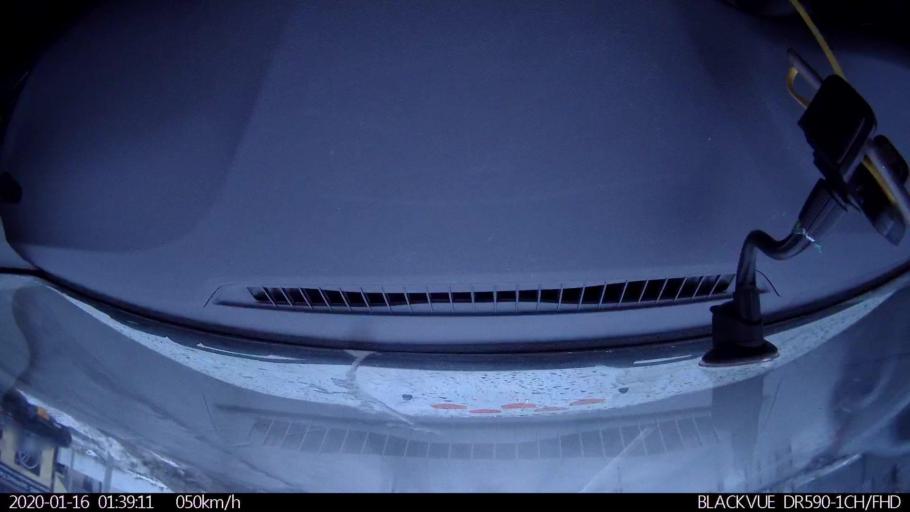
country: RU
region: Nizjnij Novgorod
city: Gorbatovka
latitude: 56.3355
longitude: 43.7972
